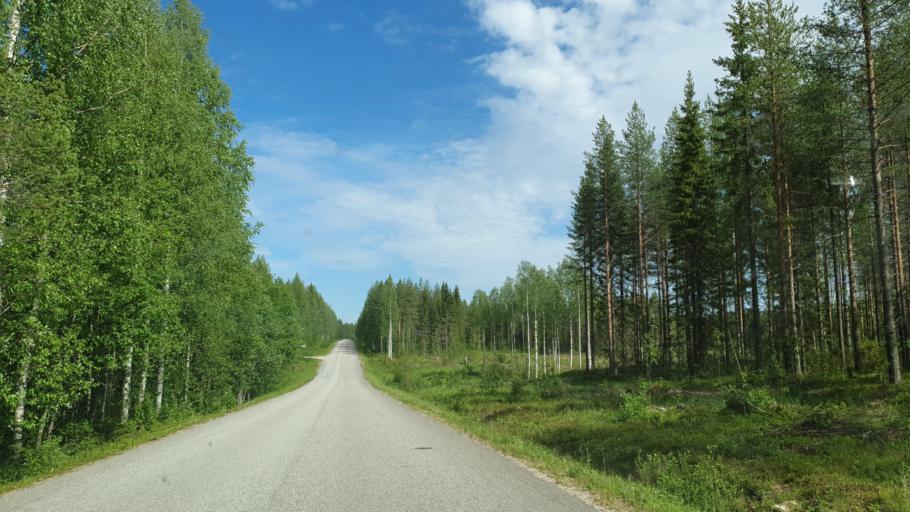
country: FI
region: Kainuu
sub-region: Kehys-Kainuu
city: Kuhmo
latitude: 64.5376
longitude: 29.2996
